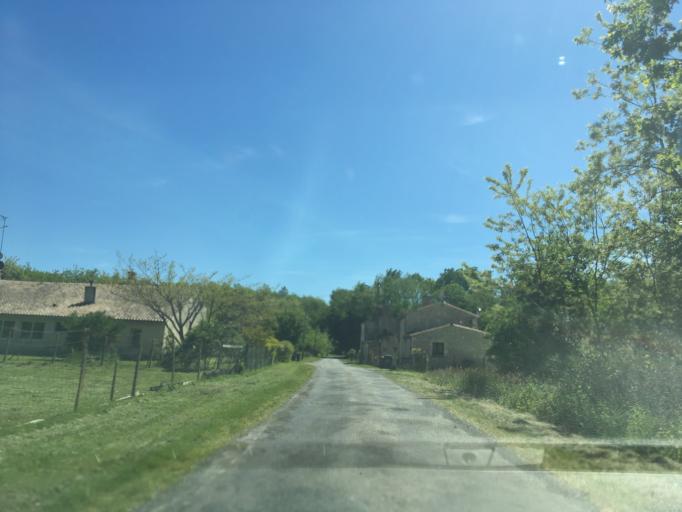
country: FR
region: Aquitaine
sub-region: Departement de la Gironde
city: Lesparre-Medoc
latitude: 45.2891
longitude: -0.8965
